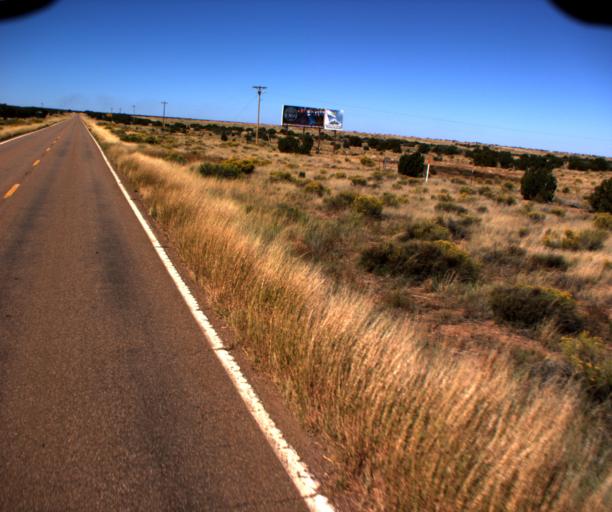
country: US
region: Arizona
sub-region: Navajo County
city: Heber-Overgaard
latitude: 34.4604
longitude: -110.4034
